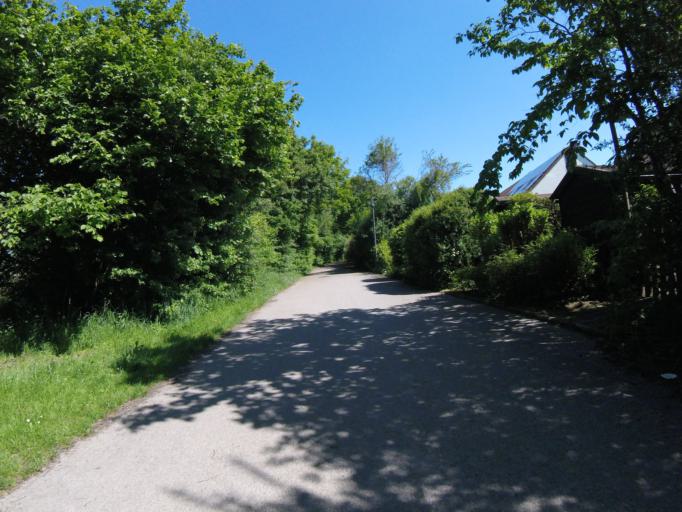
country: DE
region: Bavaria
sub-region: Upper Bavaria
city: Neubiberg
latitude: 48.0867
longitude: 11.6332
